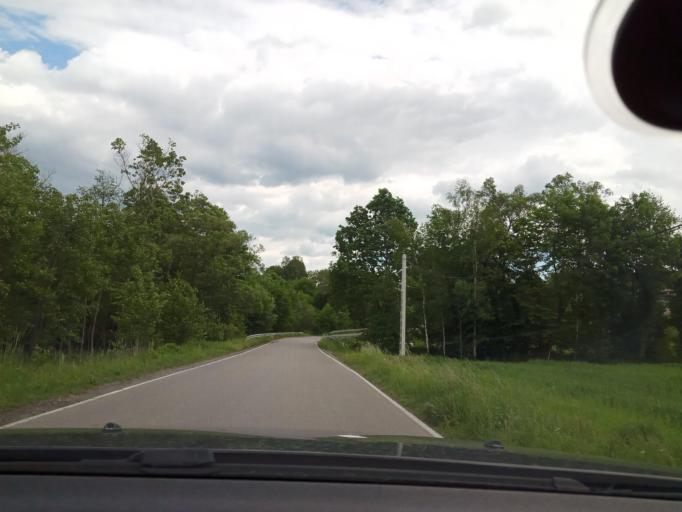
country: PL
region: Lesser Poland Voivodeship
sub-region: Powiat bochenski
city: Lapanow
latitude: 49.8253
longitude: 20.3053
